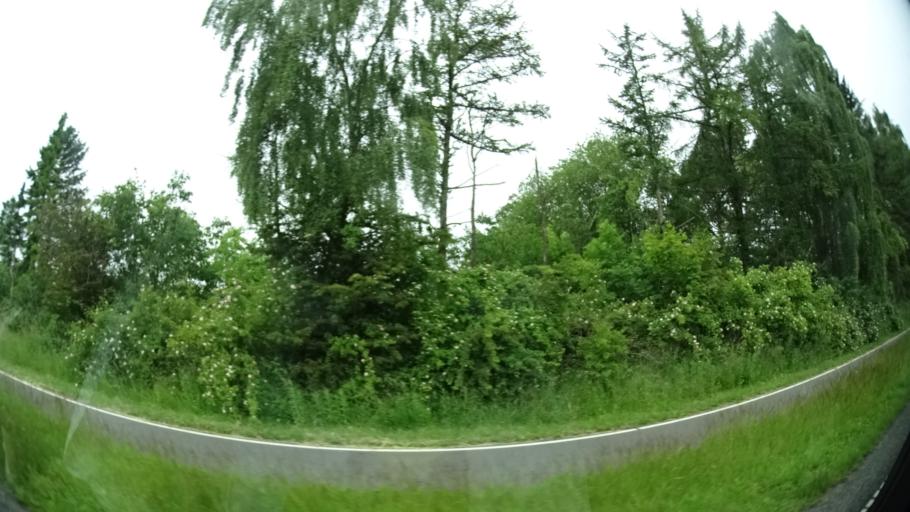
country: DK
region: Central Jutland
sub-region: Arhus Kommune
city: Hjortshoj
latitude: 56.2321
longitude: 10.2953
